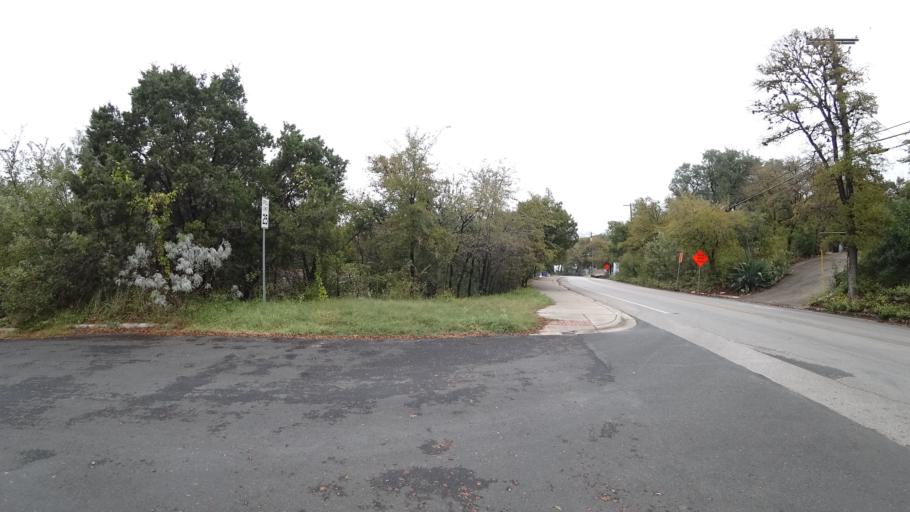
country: US
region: Texas
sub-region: Travis County
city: Rollingwood
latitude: 30.2594
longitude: -97.7723
